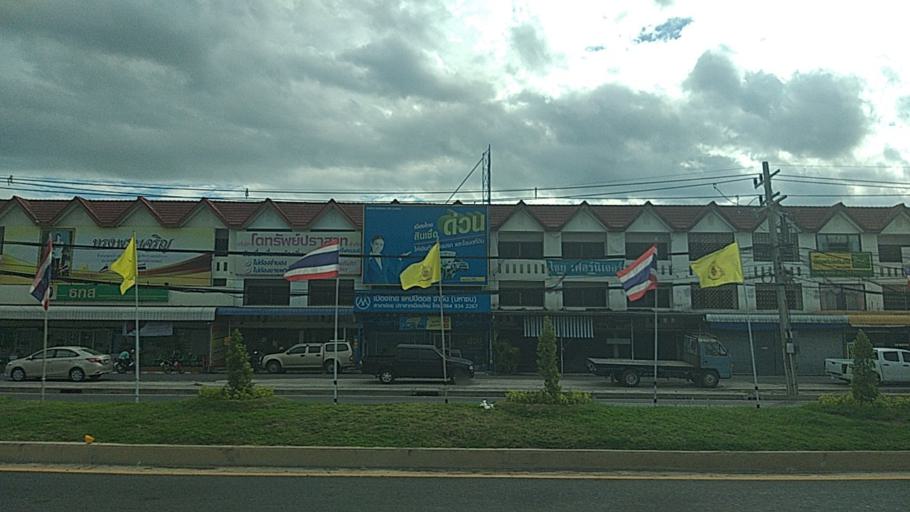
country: TH
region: Surin
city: Prasat
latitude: 14.6297
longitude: 103.4090
